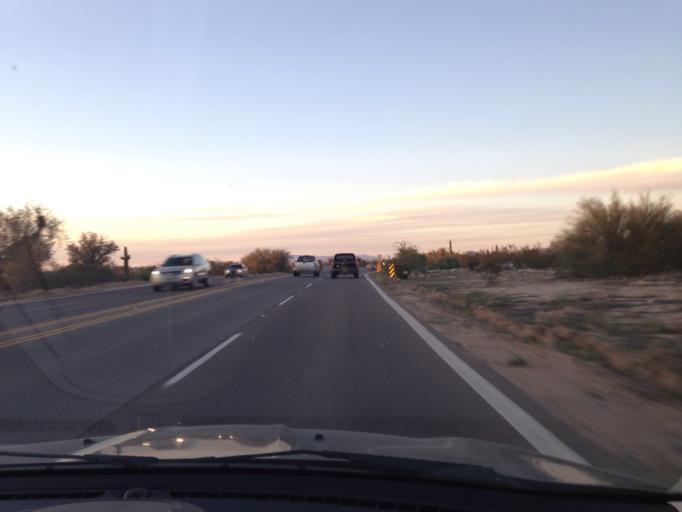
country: US
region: Arizona
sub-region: Maricopa County
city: Cave Creek
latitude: 33.7125
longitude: -111.9749
